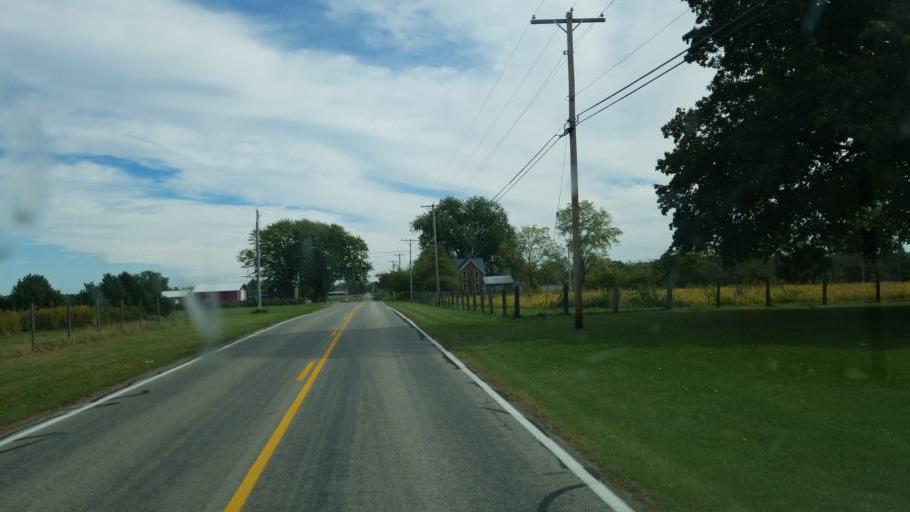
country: US
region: Ohio
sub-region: Erie County
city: Huron
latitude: 41.3648
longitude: -82.4899
